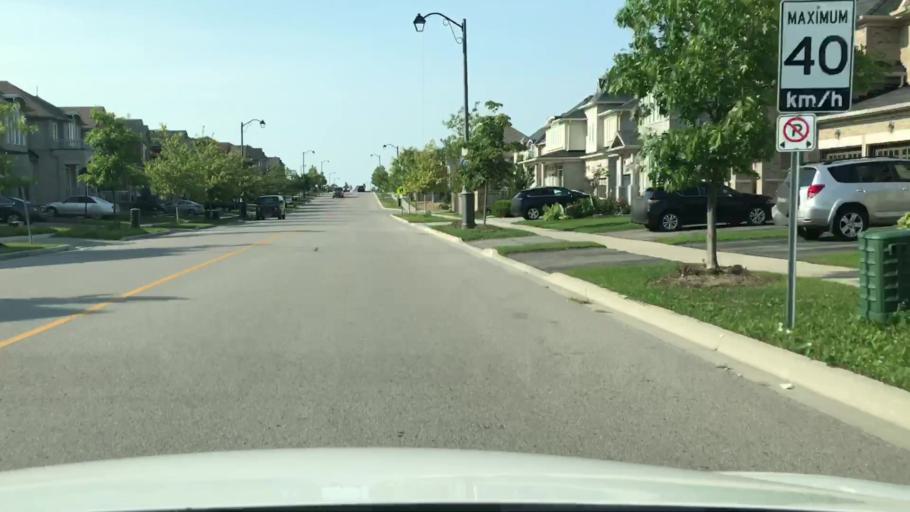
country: CA
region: Ontario
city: Newmarket
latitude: 44.0180
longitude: -79.4395
